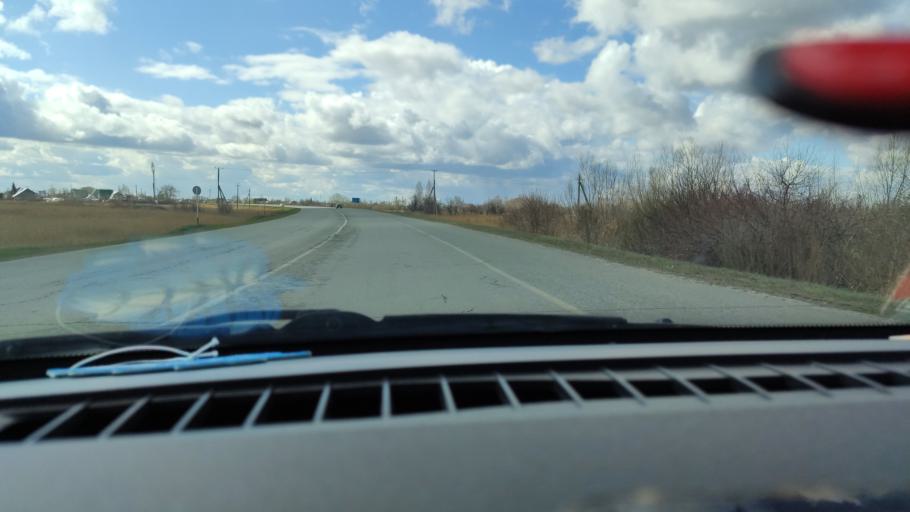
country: RU
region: Samara
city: Tol'yatti
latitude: 53.7143
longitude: 49.4242
